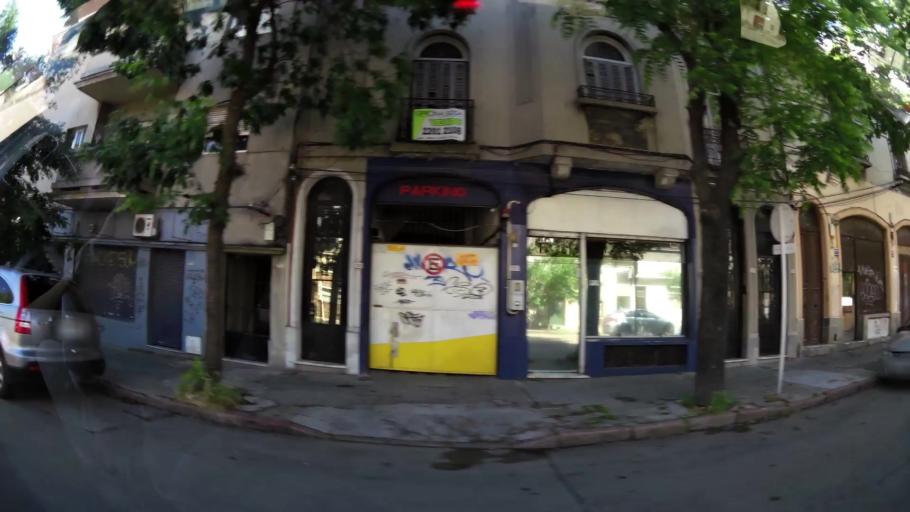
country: UY
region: Montevideo
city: Montevideo
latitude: -34.8773
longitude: -56.1873
